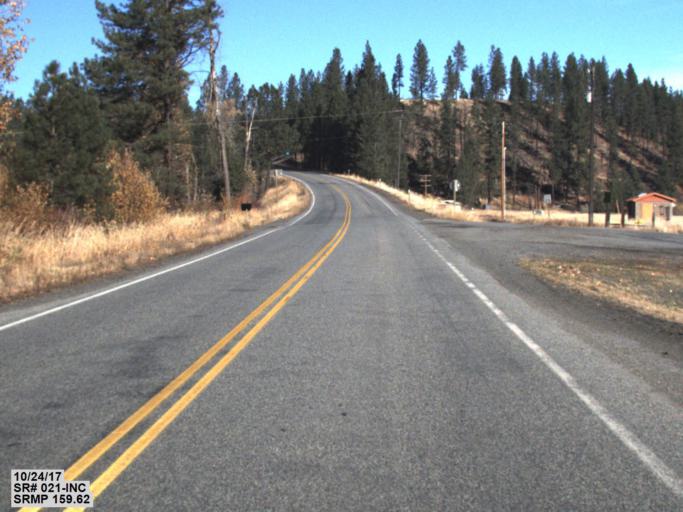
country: US
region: Washington
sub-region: Ferry County
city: Republic
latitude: 48.6341
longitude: -118.7299
